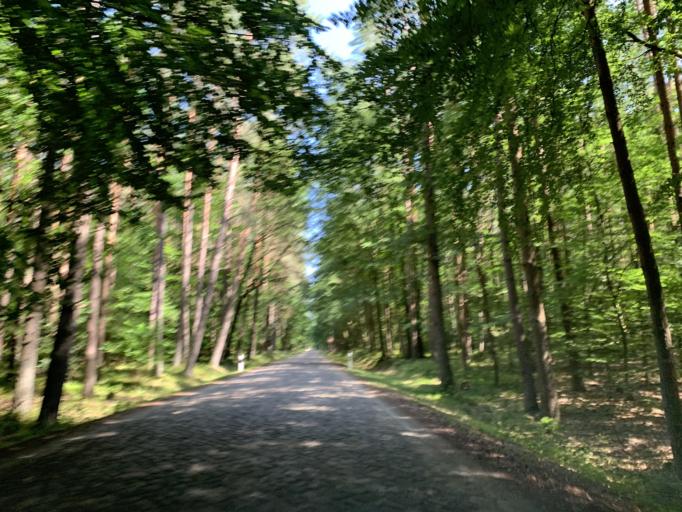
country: DE
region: Mecklenburg-Vorpommern
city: Carpin
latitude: 53.3171
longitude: 13.3092
